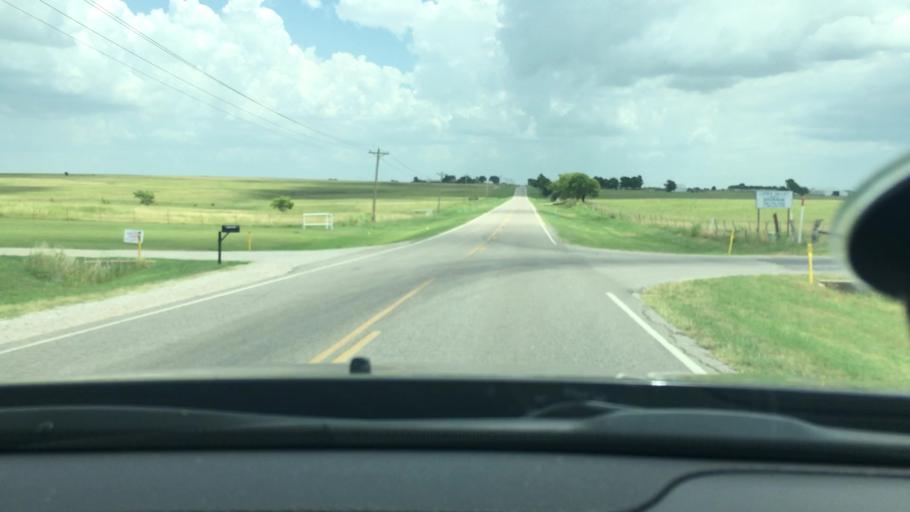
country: US
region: Oklahoma
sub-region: Love County
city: Marietta
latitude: 33.9403
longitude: -97.0745
